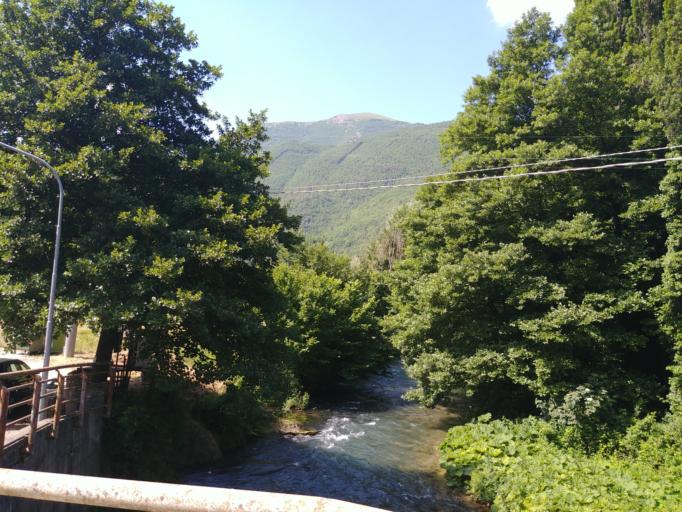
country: IT
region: Umbria
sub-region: Provincia di Perugia
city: Scheggino
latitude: 42.6848
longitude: 12.8201
